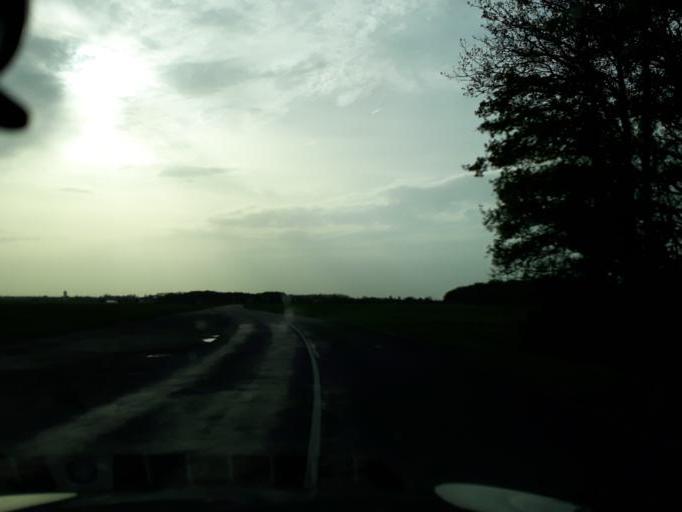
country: FR
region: Centre
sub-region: Departement du Loir-et-Cher
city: Muides-sur-Loire
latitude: 47.6604
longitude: 1.5399
